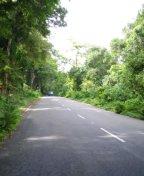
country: IN
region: Kerala
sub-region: Thrissur District
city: Trichur
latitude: 10.5278
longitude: 76.3496
